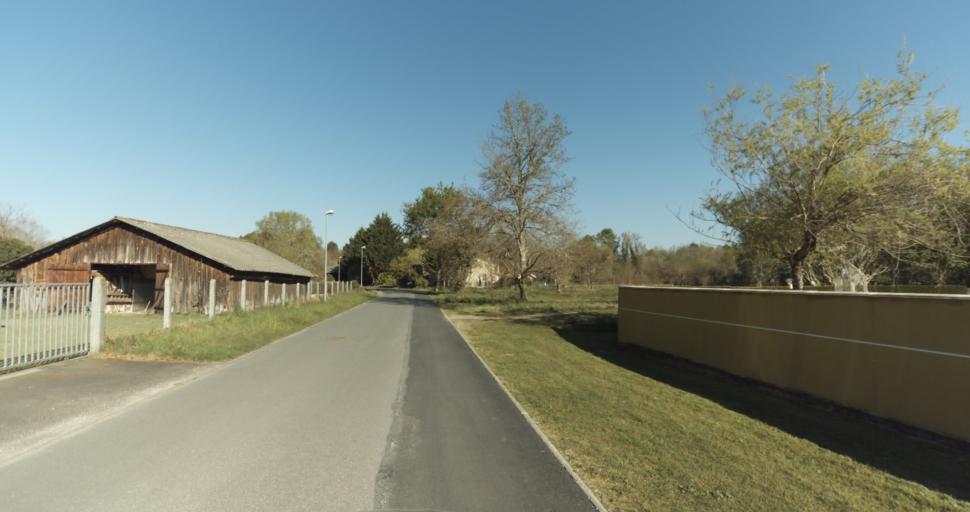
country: FR
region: Aquitaine
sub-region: Departement de la Gironde
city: Martignas-sur-Jalle
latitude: 44.8038
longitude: -0.8410
